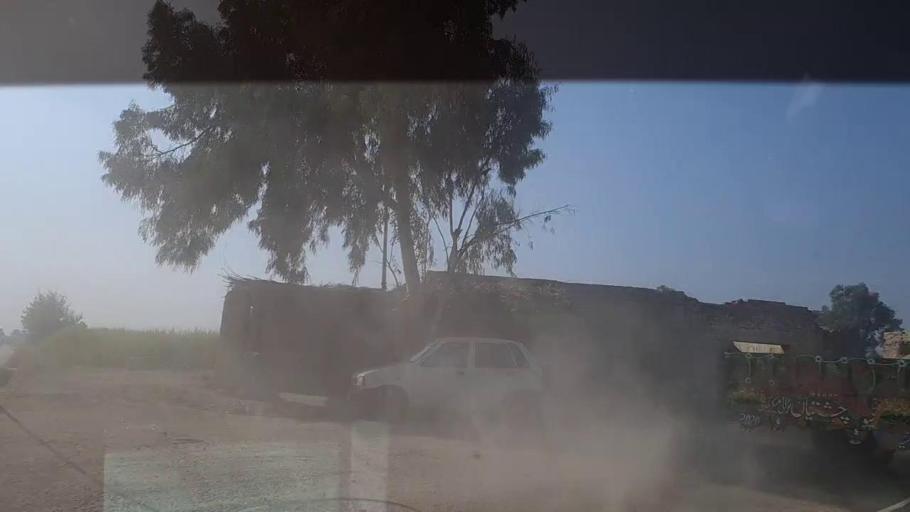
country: PK
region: Sindh
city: Kot Diji
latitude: 27.4374
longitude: 68.6349
